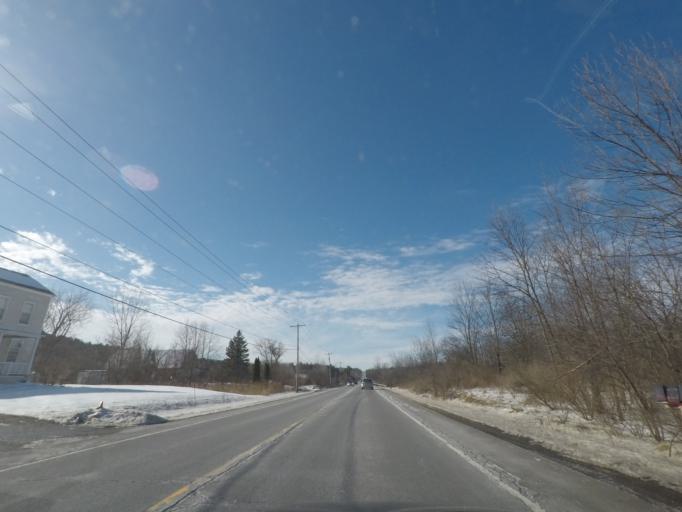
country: US
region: New York
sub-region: Albany County
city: Altamont
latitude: 42.7426
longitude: -74.0238
